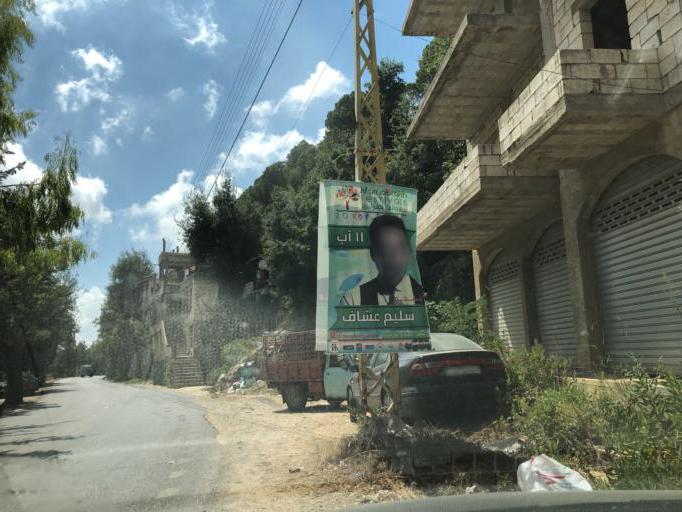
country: LB
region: Mont-Liban
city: Beit ed Dine
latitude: 33.7007
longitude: 35.5953
